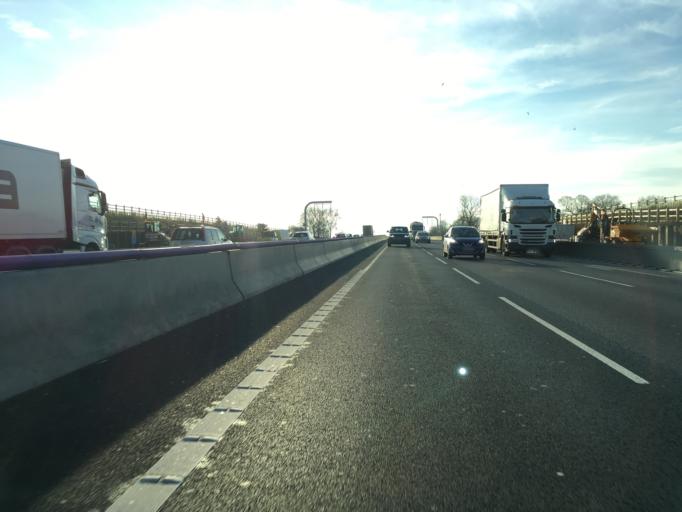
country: GB
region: England
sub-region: Cheshire East
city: Sandbach
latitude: 53.1261
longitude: -2.3355
